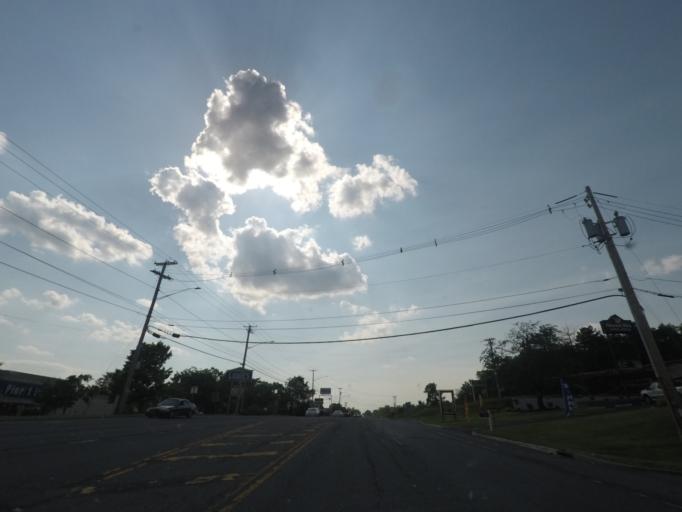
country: US
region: New York
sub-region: Orange County
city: Gardnertown
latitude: 41.5048
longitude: -74.0706
